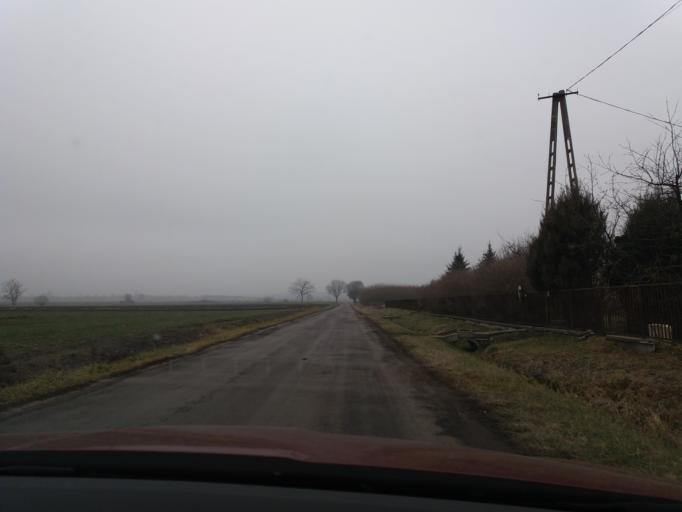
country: HU
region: Vas
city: Janoshaza
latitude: 47.0968
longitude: 17.2189
